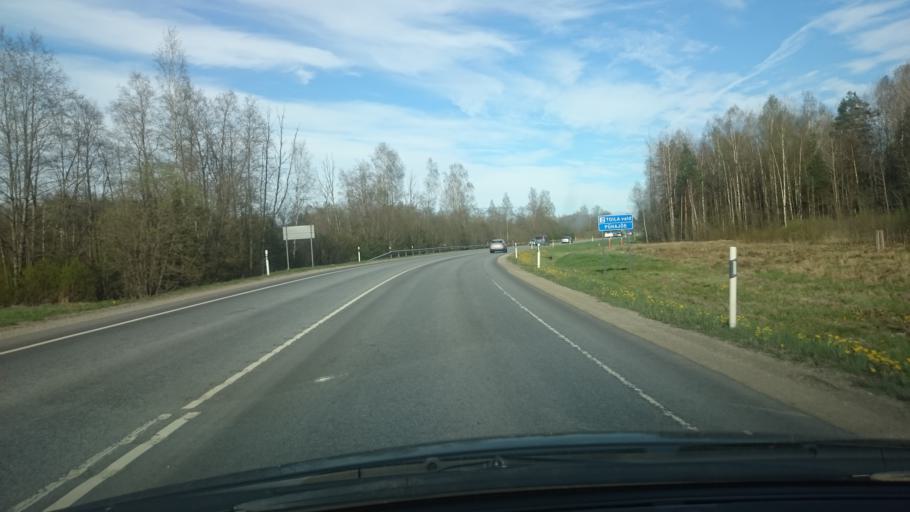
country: EE
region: Ida-Virumaa
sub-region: Toila vald
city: Toila
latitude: 59.3737
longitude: 27.4967
